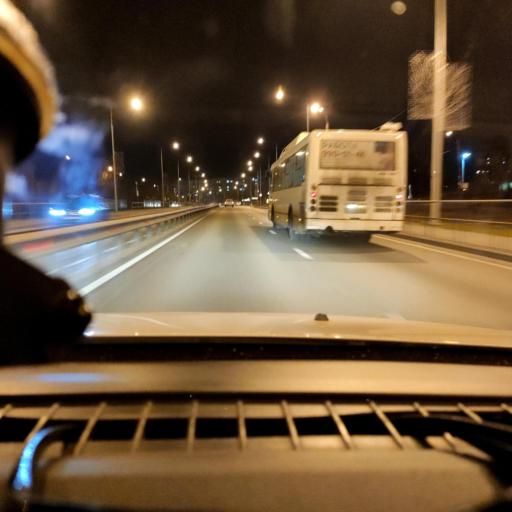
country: RU
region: Samara
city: Volzhskiy
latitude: 53.3555
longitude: 50.2097
